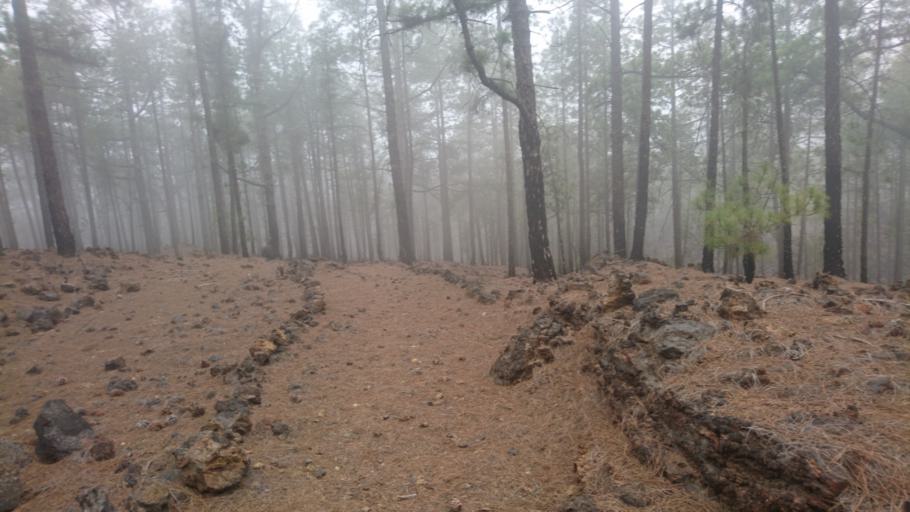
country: ES
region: Canary Islands
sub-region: Provincia de Santa Cruz de Tenerife
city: Guia de Isora
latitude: 28.2502
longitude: -16.7717
